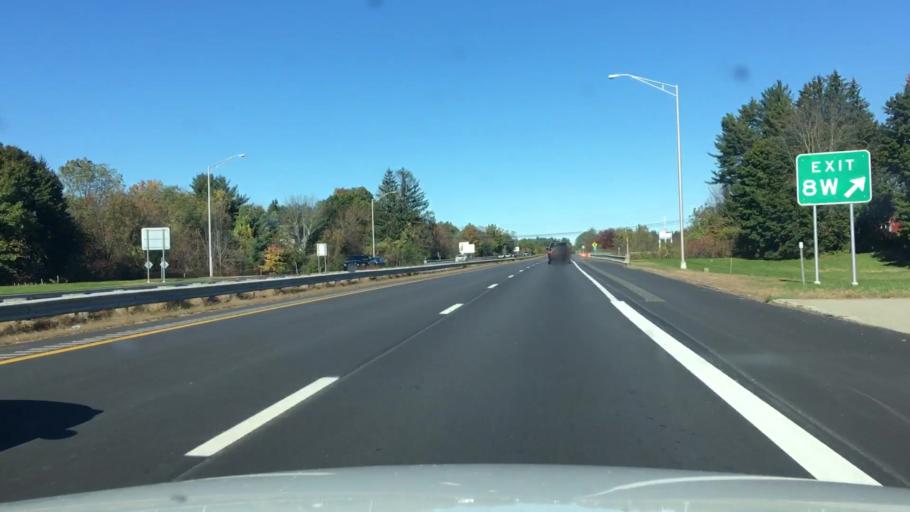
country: US
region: New Hampshire
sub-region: Strafford County
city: Dover
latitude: 43.1859
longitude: -70.8876
